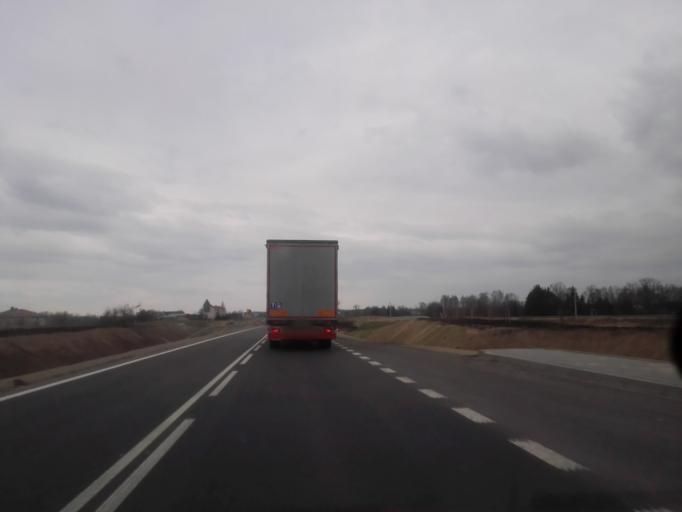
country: PL
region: Podlasie
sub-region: Powiat augustowski
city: Augustow
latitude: 53.7851
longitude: 22.8504
